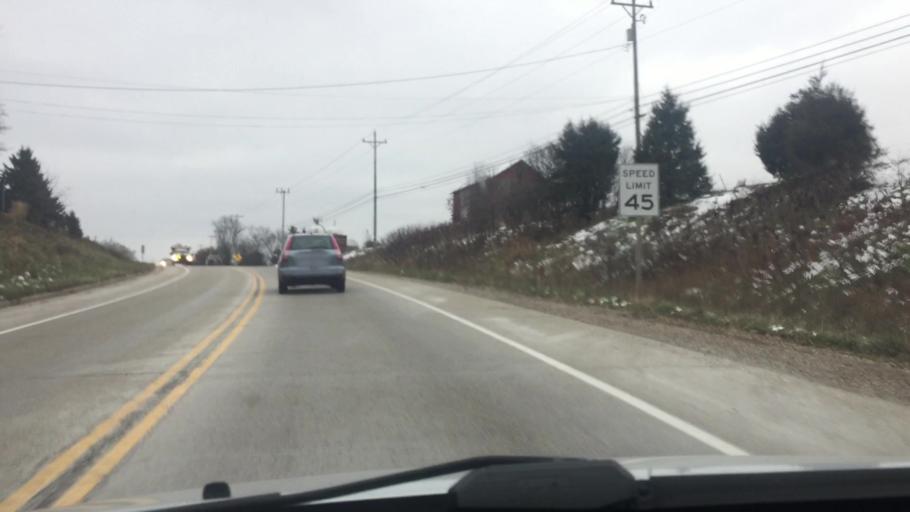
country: US
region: Wisconsin
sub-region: Waukesha County
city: Hartland
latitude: 43.0724
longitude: -88.3651
